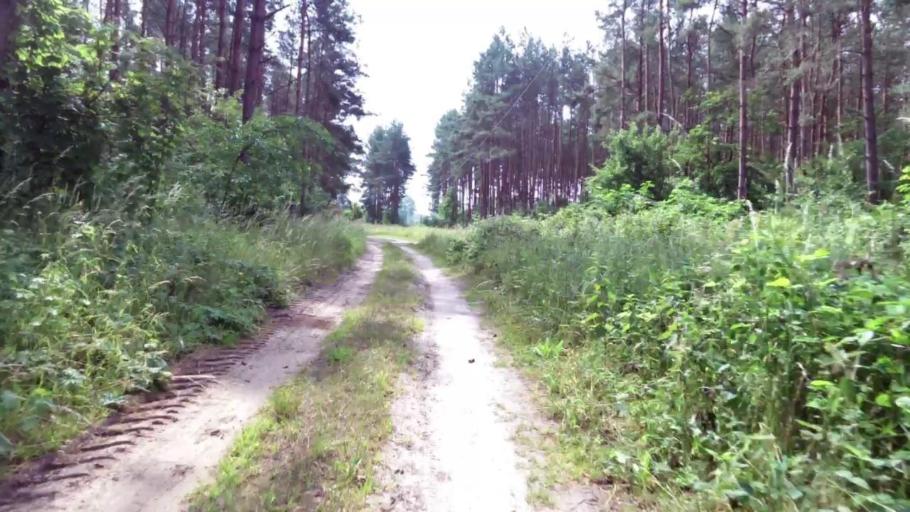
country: PL
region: West Pomeranian Voivodeship
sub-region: Powiat kamienski
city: Wolin
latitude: 53.7687
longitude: 14.6447
